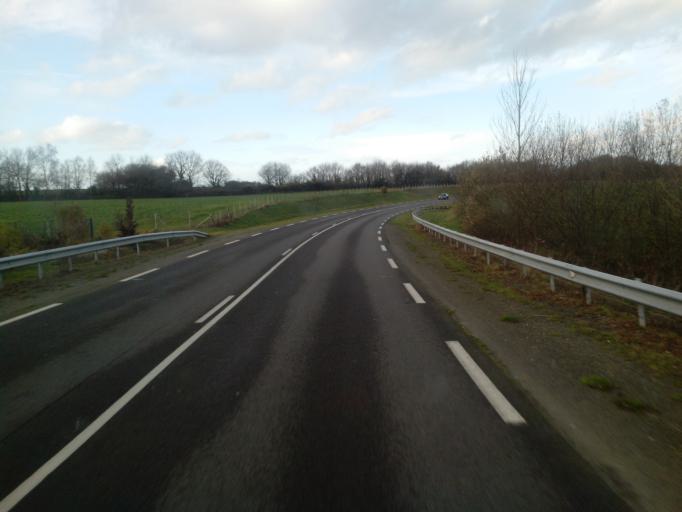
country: FR
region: Brittany
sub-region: Departement d'Ille-et-Vilaine
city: Pleurtuit
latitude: 48.5969
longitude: -2.0699
